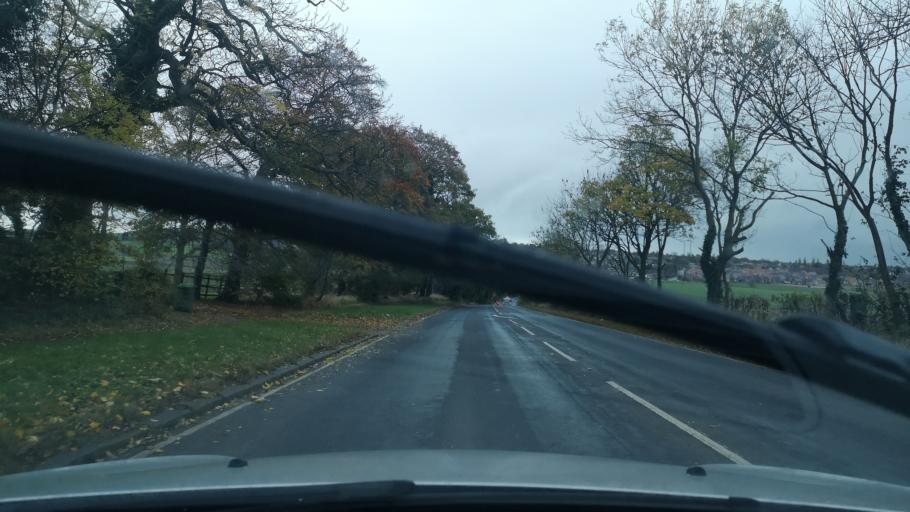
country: GB
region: England
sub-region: City and Borough of Wakefield
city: Low Ackworth
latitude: 53.6675
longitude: -1.3248
